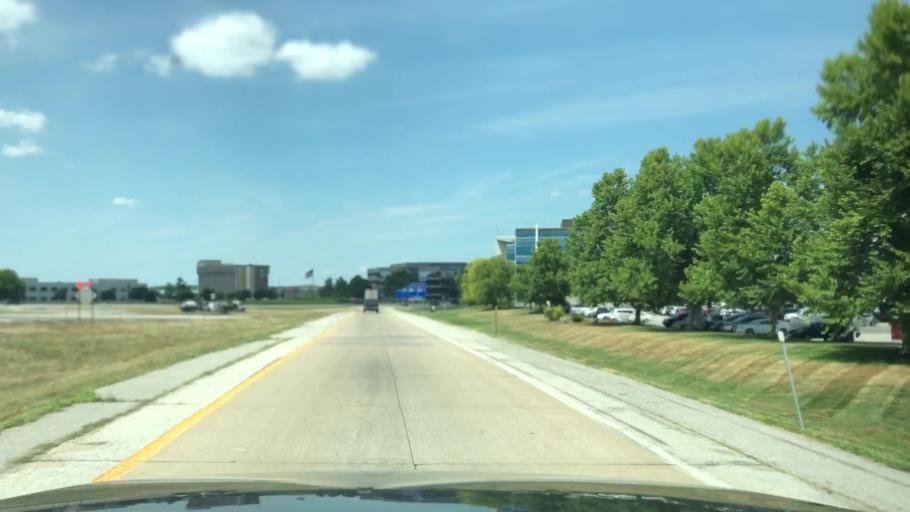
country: US
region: Missouri
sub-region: Saint Charles County
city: Saint Charles
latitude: 38.7559
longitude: -90.4559
